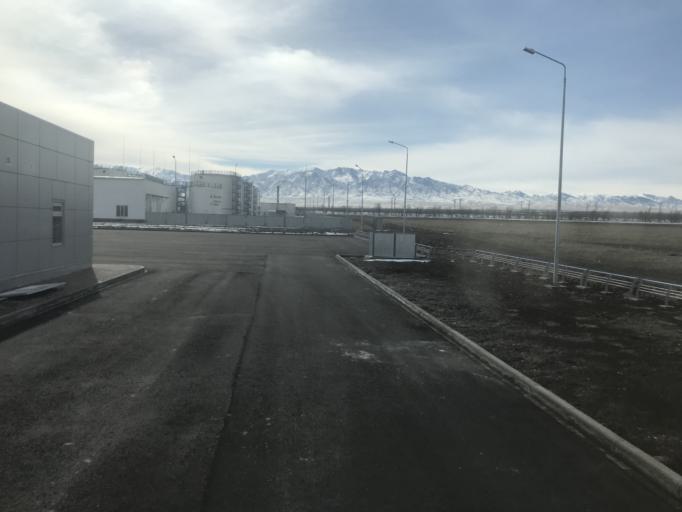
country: KZ
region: Zhambyl
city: Sarykemer
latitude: 43.0084
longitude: 71.7847
